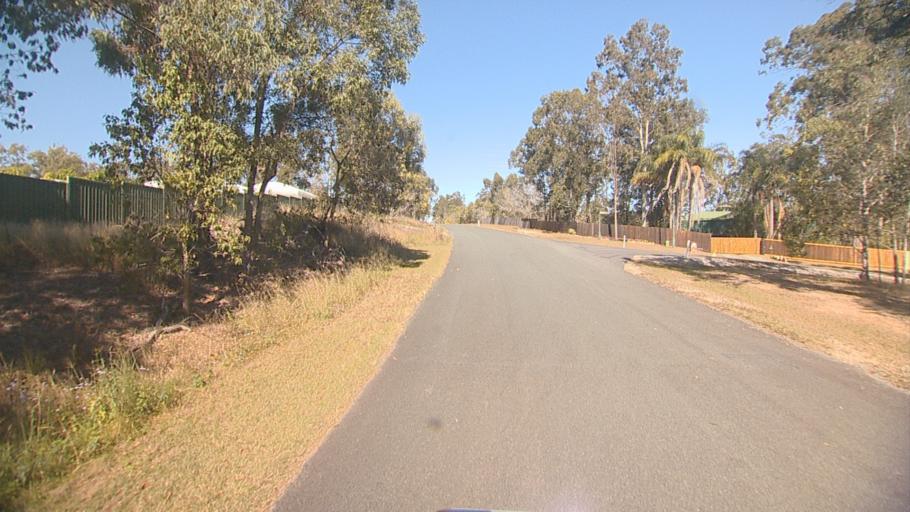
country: AU
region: Queensland
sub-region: Ipswich
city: Springfield Lakes
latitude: -27.7165
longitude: 152.9306
